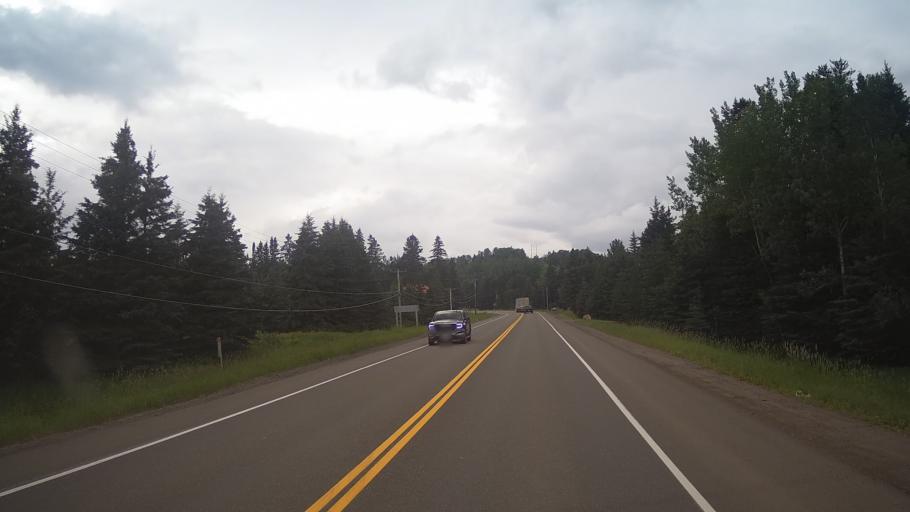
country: CA
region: Ontario
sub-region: Thunder Bay District
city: Thunder Bay
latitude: 48.4956
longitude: -89.4036
